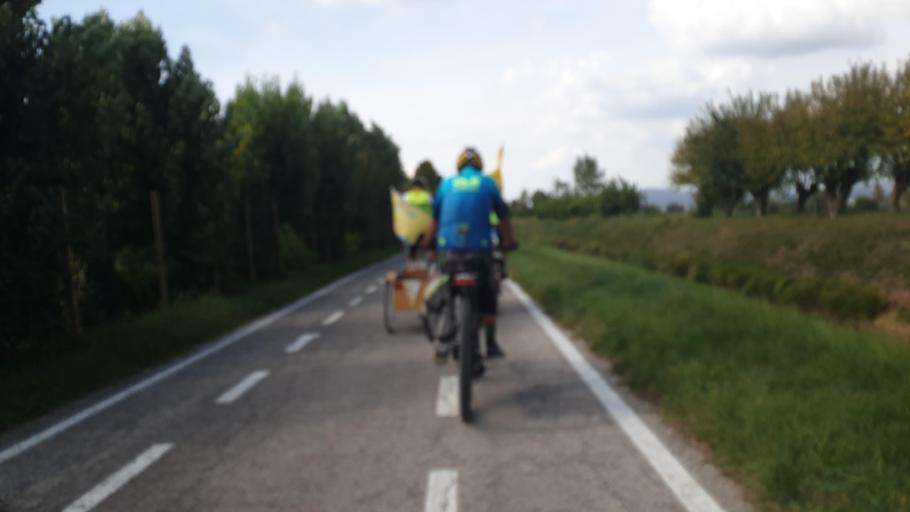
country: IT
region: Veneto
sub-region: Provincia di Vicenza
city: Agugliaro
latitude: 45.3315
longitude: 11.5720
